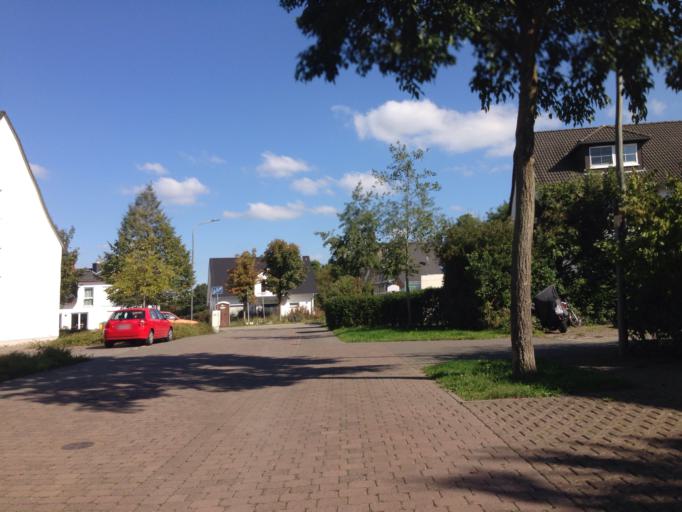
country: DE
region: Hesse
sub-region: Regierungsbezirk Giessen
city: Giessen
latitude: 50.6053
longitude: 8.6774
